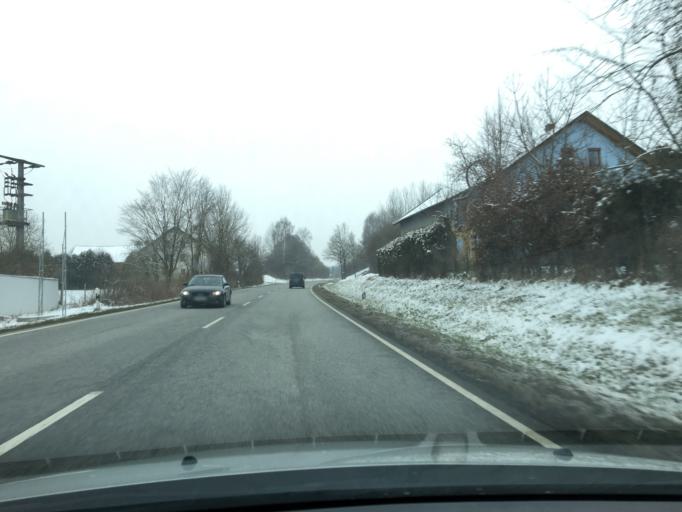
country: DE
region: Bavaria
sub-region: Lower Bavaria
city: Furth
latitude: 48.4263
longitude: 12.4013
